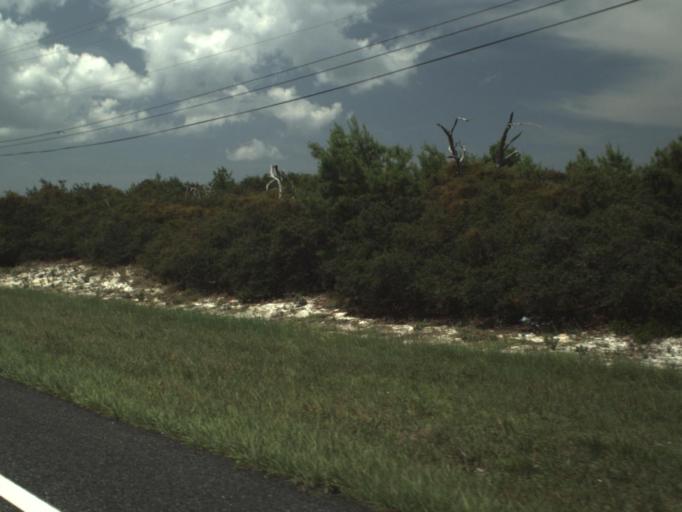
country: US
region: Florida
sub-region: Palm Beach County
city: Tequesta
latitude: 27.0088
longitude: -80.1022
